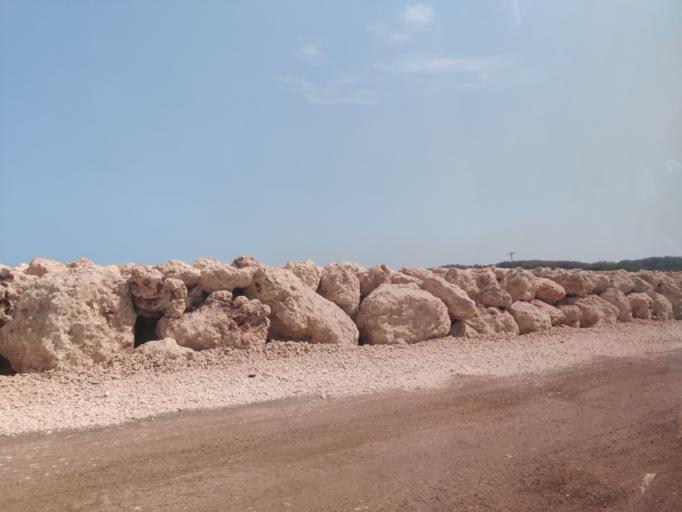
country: CO
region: Bolivar
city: Turbana
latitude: 10.1898
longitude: -75.6357
